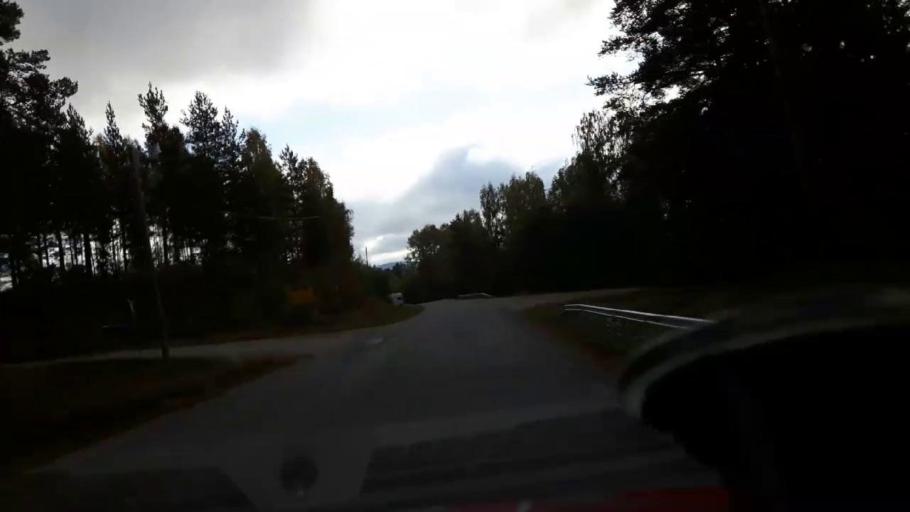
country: SE
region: Gaevleborg
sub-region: Ljusdals Kommun
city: Farila
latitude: 61.7823
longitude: 15.9399
